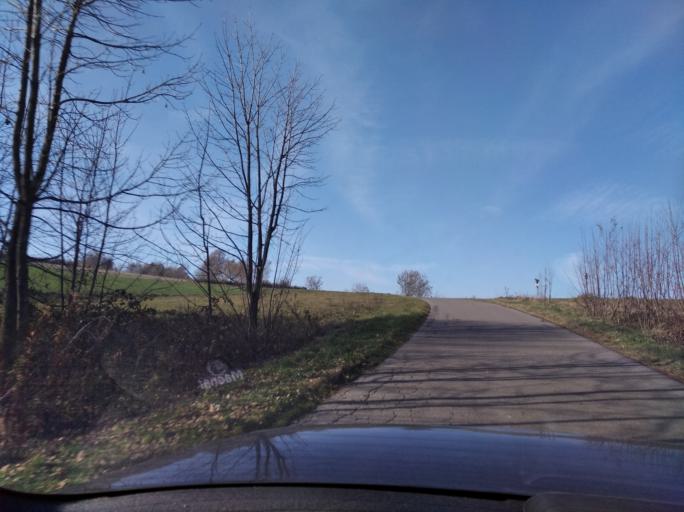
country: PL
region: Subcarpathian Voivodeship
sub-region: Powiat ropczycko-sedziszowski
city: Wielopole Skrzynskie
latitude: 49.9012
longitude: 21.5845
